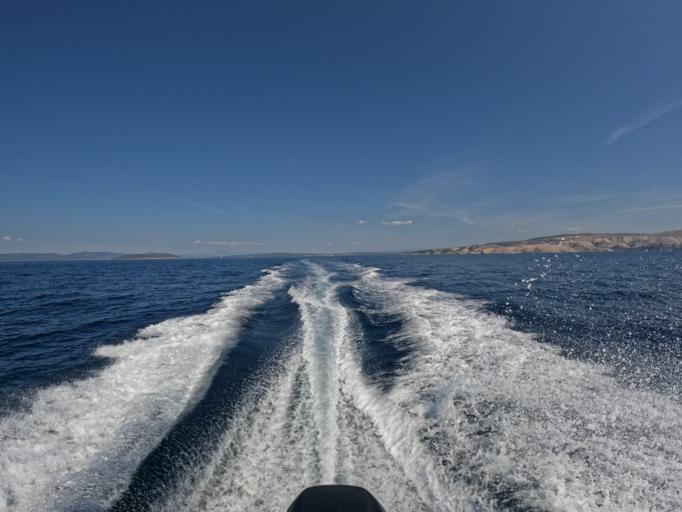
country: HR
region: Primorsko-Goranska
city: Punat
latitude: 44.9163
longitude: 14.6247
